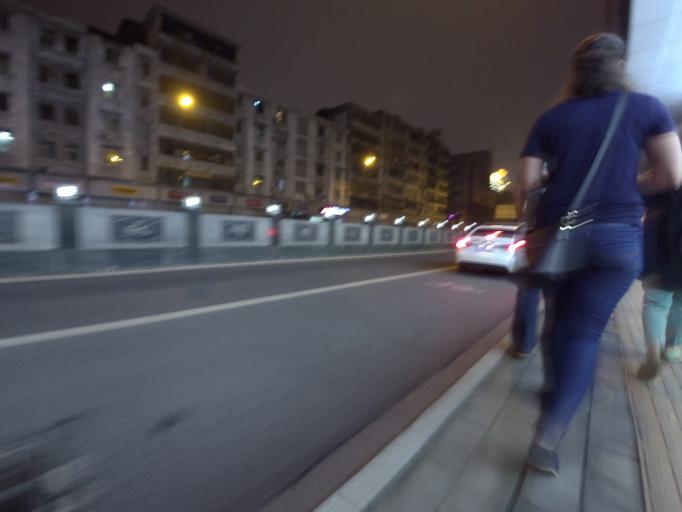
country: CN
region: Sichuan
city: Chengdu
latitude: 30.6681
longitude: 104.0581
